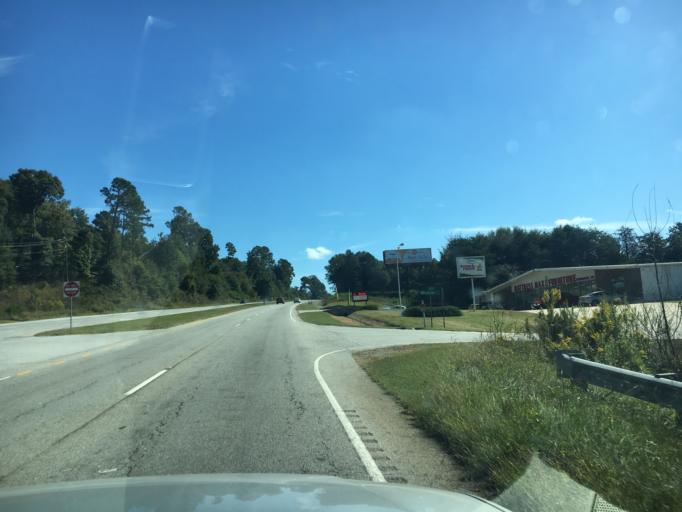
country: US
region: South Carolina
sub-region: Spartanburg County
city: Fairforest
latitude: 34.9398
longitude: -82.0529
